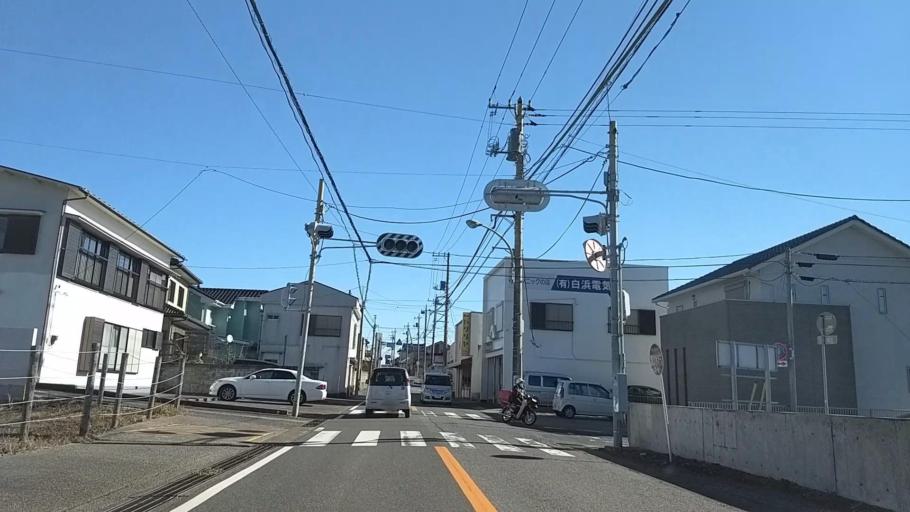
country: JP
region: Chiba
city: Tateyama
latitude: 34.9078
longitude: 139.8981
